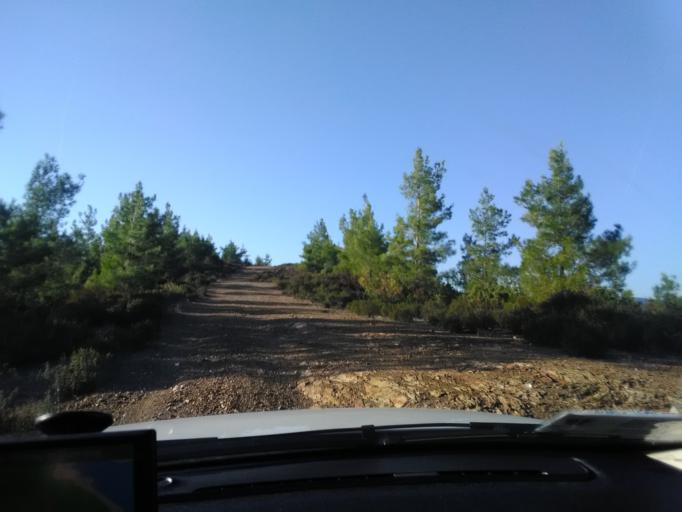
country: TR
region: Antalya
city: Gazipasa
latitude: 36.3079
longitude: 32.3967
